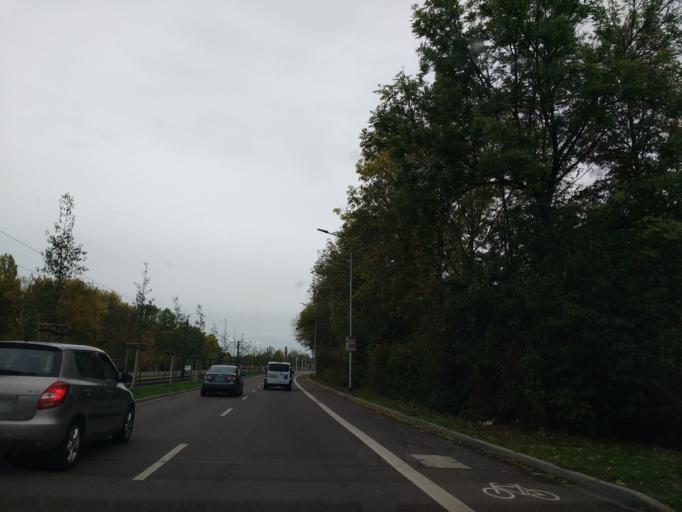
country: DE
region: Saxony-Anhalt
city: Halle Neustadt
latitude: 51.4856
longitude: 11.9461
